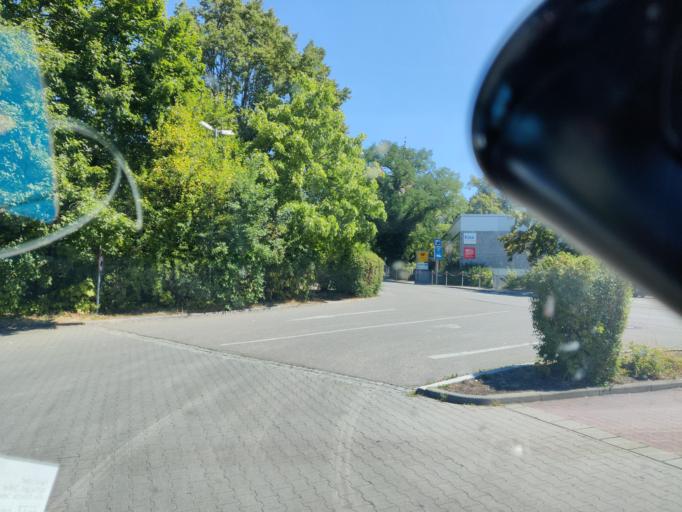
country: DE
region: Bavaria
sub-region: Regierungsbezirk Mittelfranken
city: Weissenburg in Bayern
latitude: 49.0325
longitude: 10.9684
